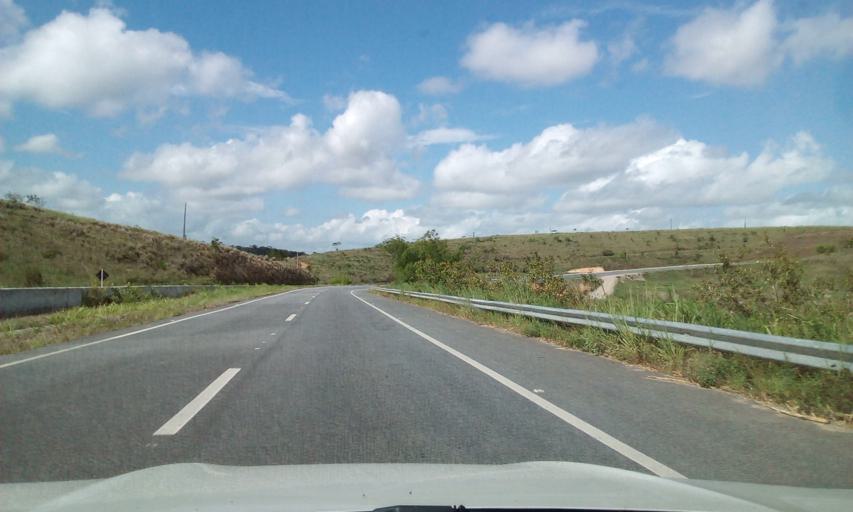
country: BR
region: Alagoas
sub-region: Rio Largo
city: Rio Largo
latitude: -9.4862
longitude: -35.8948
